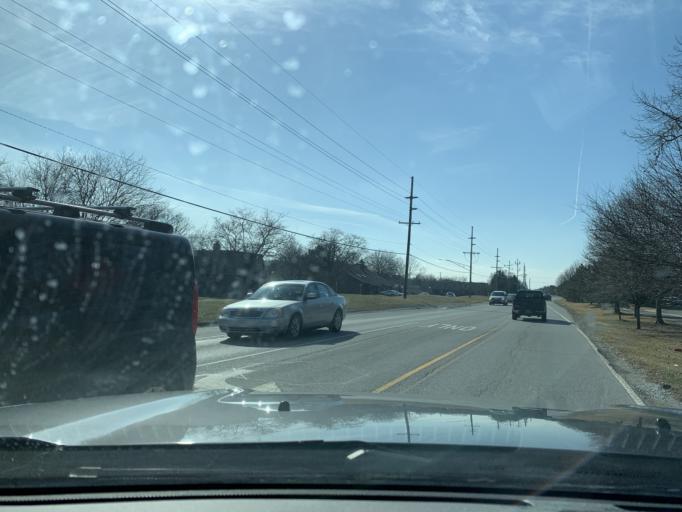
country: US
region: Indiana
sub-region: Lake County
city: Dyer
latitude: 41.5232
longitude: -87.4871
